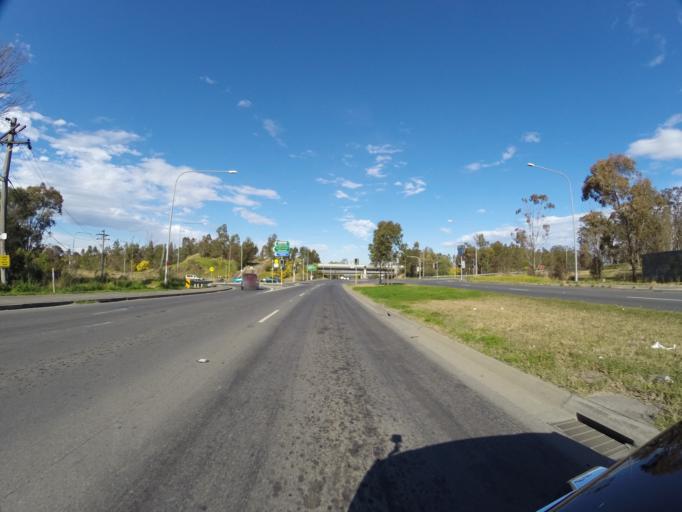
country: AU
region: New South Wales
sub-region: Fairfield
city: Cecil Park
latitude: -33.8758
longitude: 150.8420
